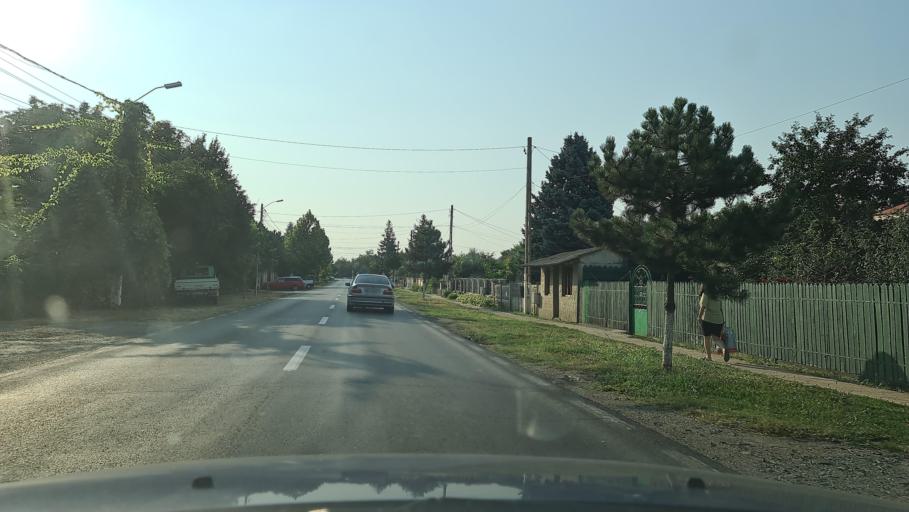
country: RO
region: Calarasi
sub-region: Comuna Dor Marunt
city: Dor Marunt
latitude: 44.4371
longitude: 26.9497
